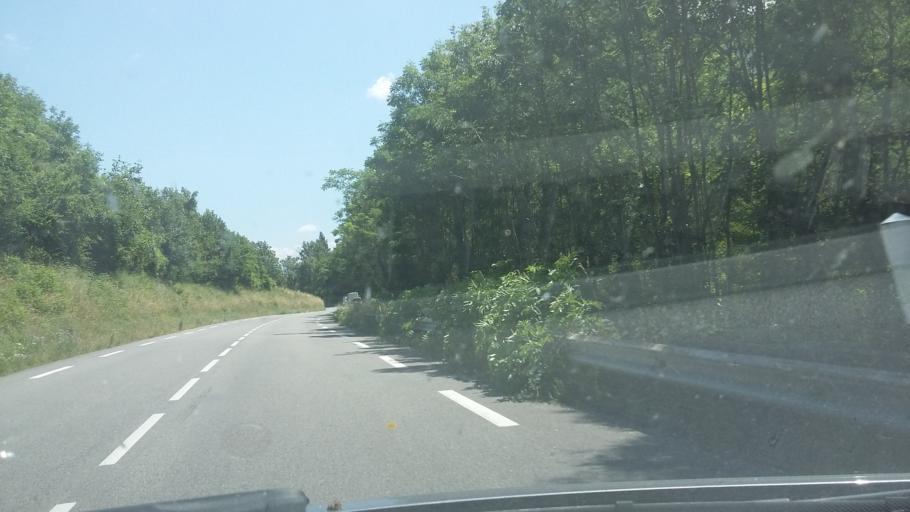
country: FR
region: Rhone-Alpes
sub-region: Departement de l'Ain
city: Tenay
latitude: 45.8476
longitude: 5.5544
